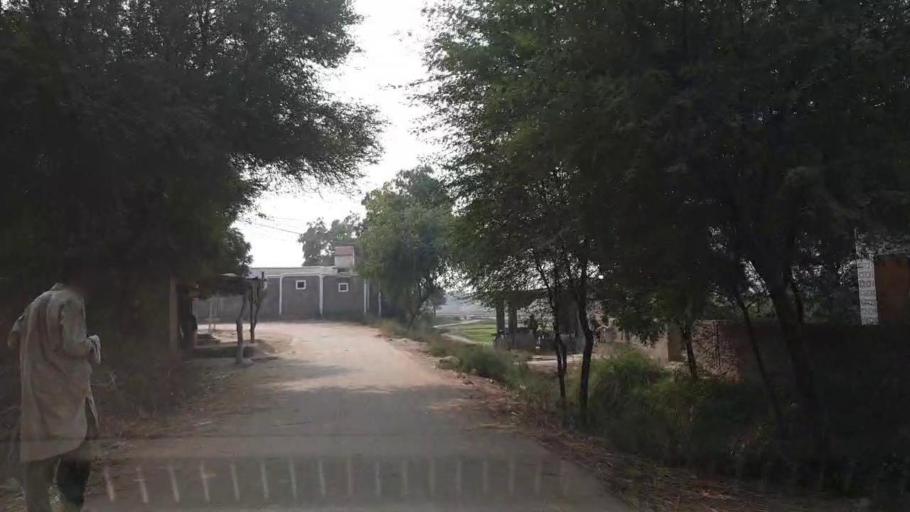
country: PK
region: Sindh
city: Tando Muhammad Khan
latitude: 25.1822
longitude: 68.6256
